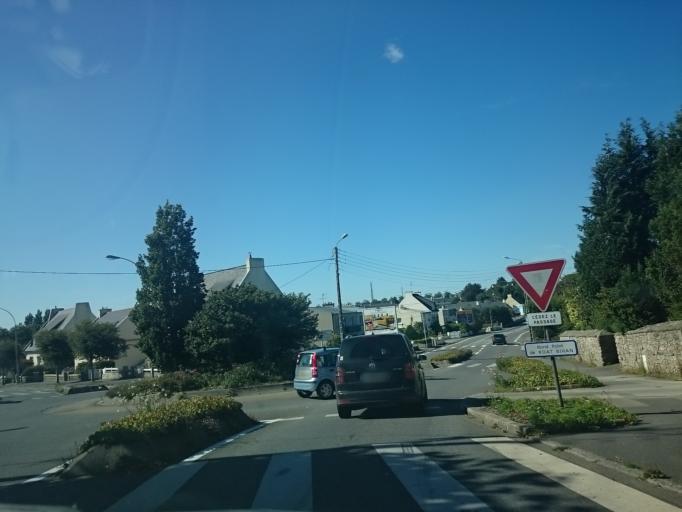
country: FR
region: Brittany
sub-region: Departement du Finistere
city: Brest
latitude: 48.4184
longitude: -4.4871
